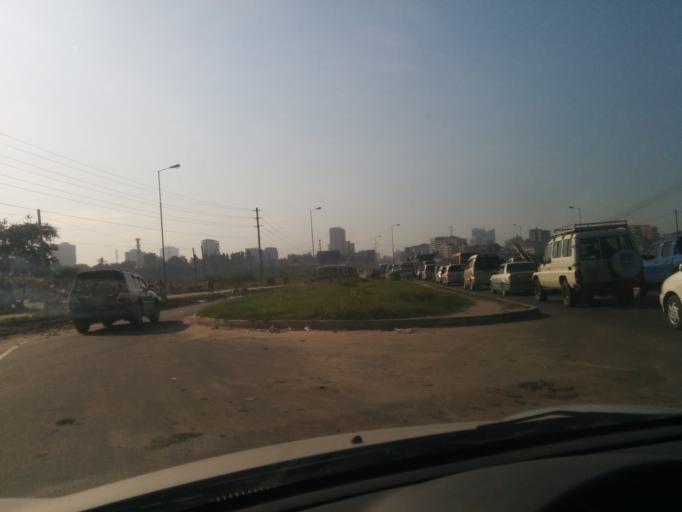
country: TZ
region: Dar es Salaam
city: Dar es Salaam
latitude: -6.8105
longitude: 39.2668
